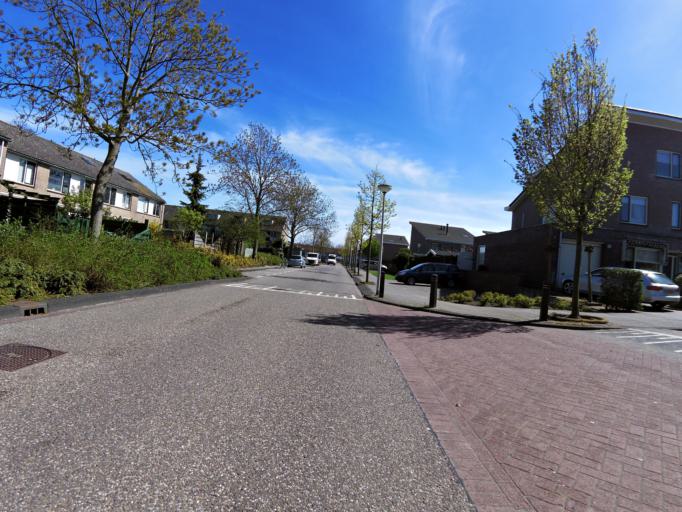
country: NL
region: South Holland
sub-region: Gemeente Brielle
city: Brielle
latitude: 51.9141
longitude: 4.1073
